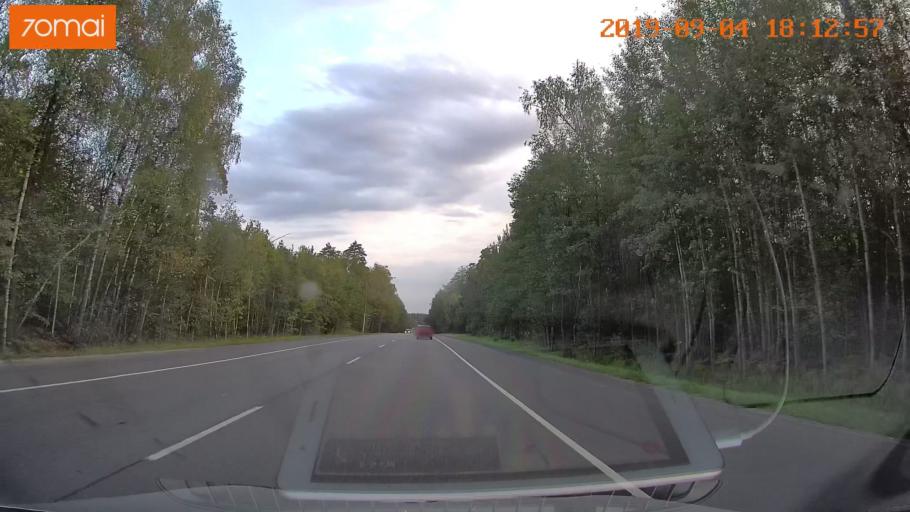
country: RU
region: Moskovskaya
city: Lopatinskiy
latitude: 55.3659
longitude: 38.7362
